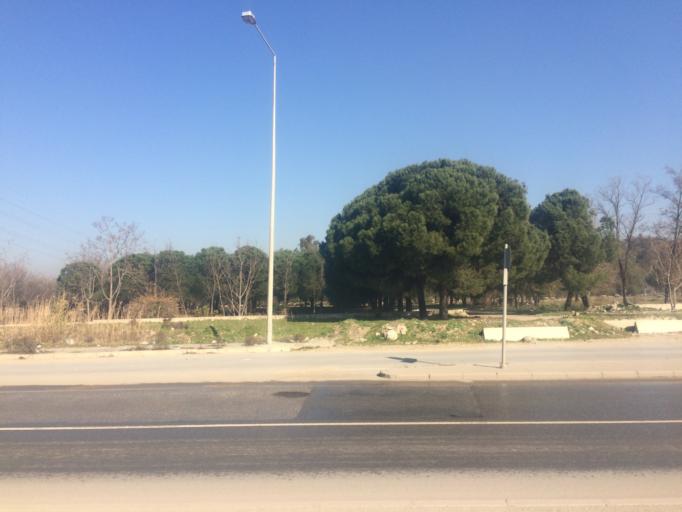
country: TR
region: Izmir
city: Menemen
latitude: 38.5183
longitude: 27.0334
